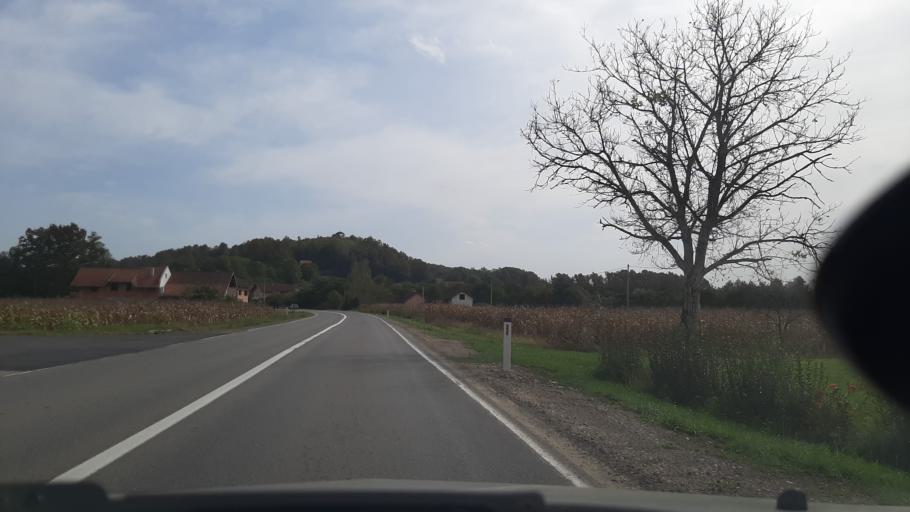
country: BA
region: Republika Srpska
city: Laktasi
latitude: 44.8755
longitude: 17.3121
